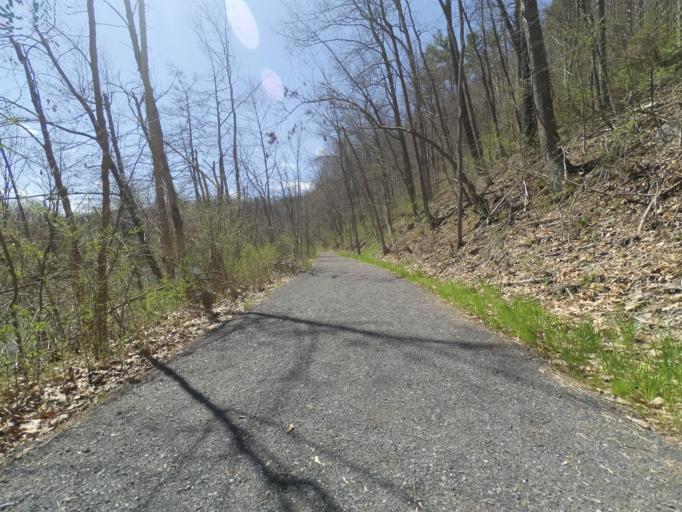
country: US
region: Pennsylvania
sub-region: Centre County
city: Houserville
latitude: 40.8576
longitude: -77.8197
